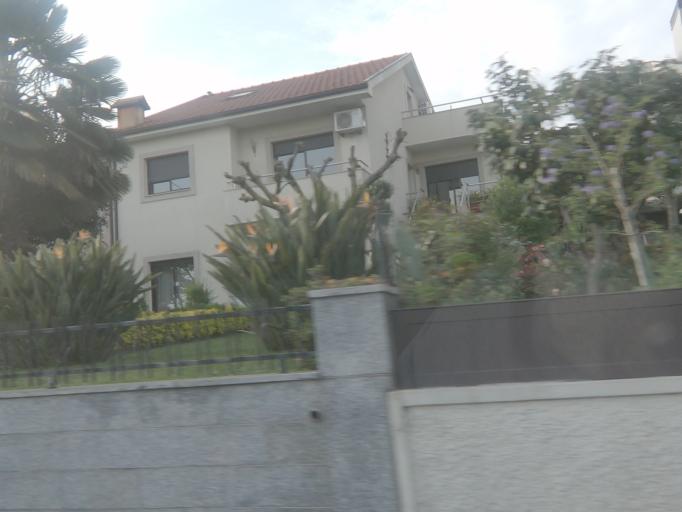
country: PT
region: Porto
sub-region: Valongo
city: Campo
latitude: 41.1822
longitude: -8.4757
